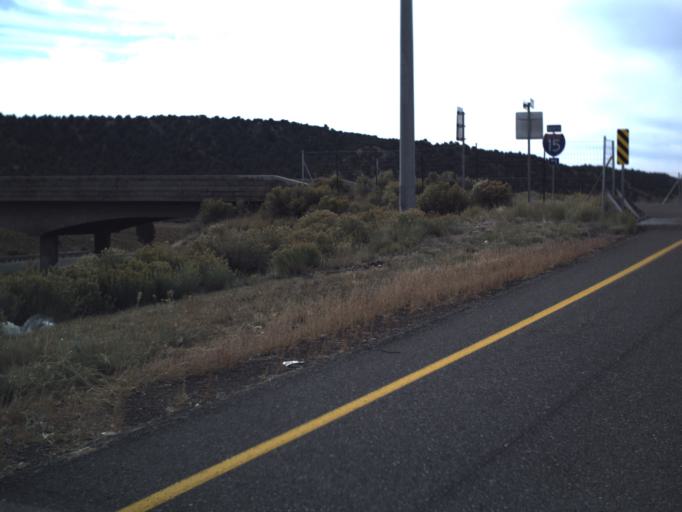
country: US
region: Utah
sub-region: Beaver County
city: Beaver
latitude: 38.4135
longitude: -112.6528
